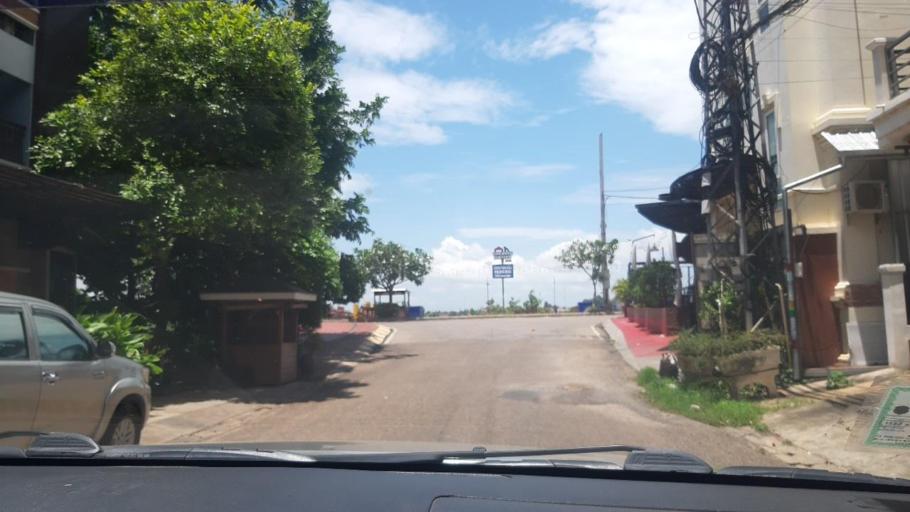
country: LA
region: Vientiane
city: Vientiane
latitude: 17.9669
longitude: 102.5932
